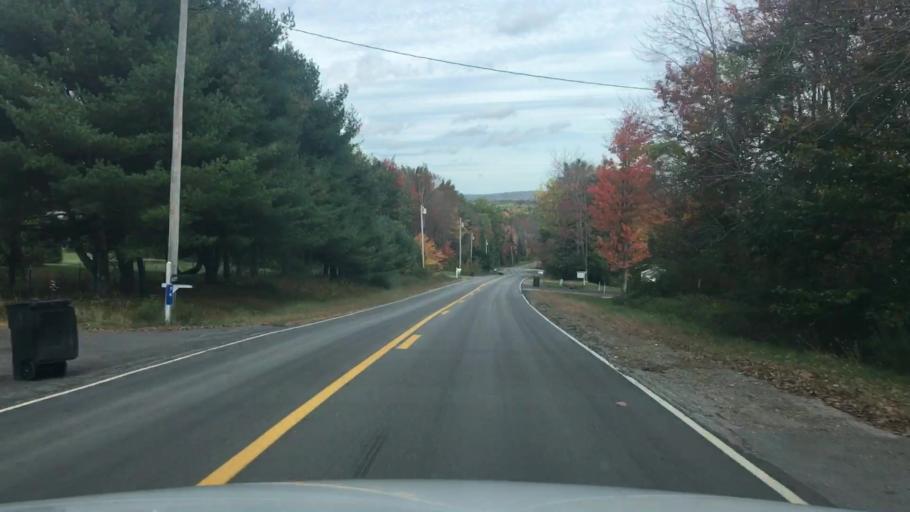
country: US
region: Maine
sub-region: Waldo County
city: Searsmont
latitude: 44.4016
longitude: -69.1370
